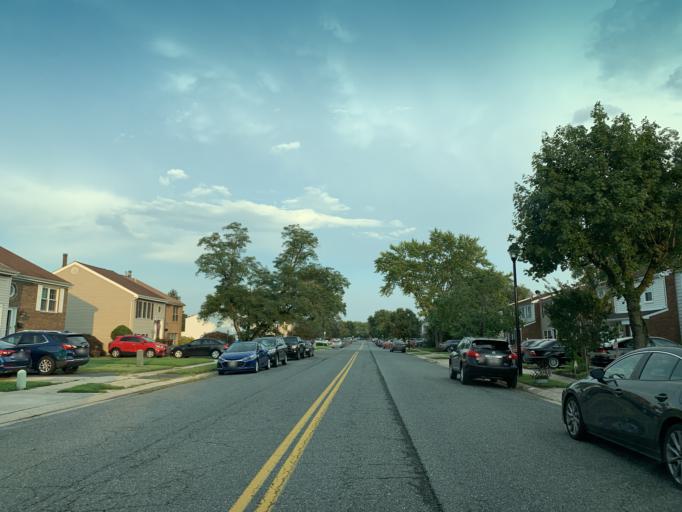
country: US
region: Maryland
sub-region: Harford County
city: Joppatowne
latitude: 39.4079
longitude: -76.3595
